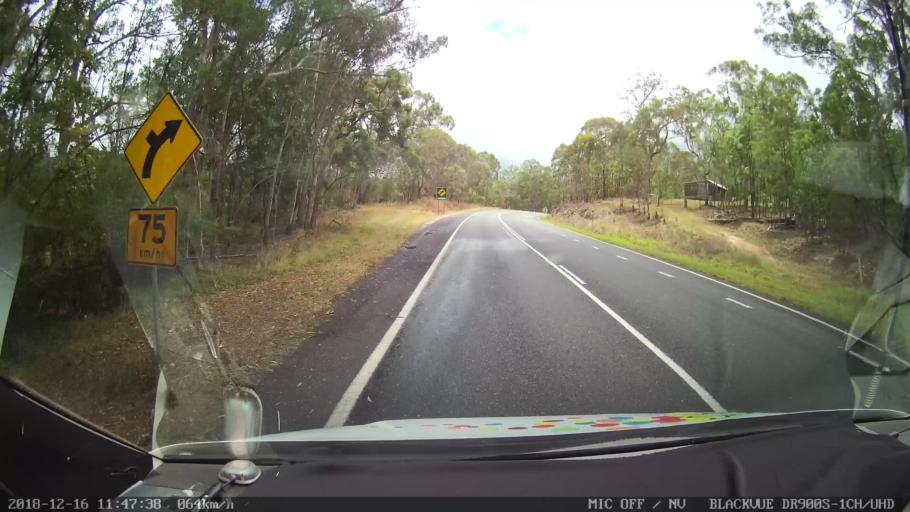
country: AU
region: New South Wales
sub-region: Tenterfield Municipality
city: Carrolls Creek
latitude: -28.9206
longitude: 152.2399
